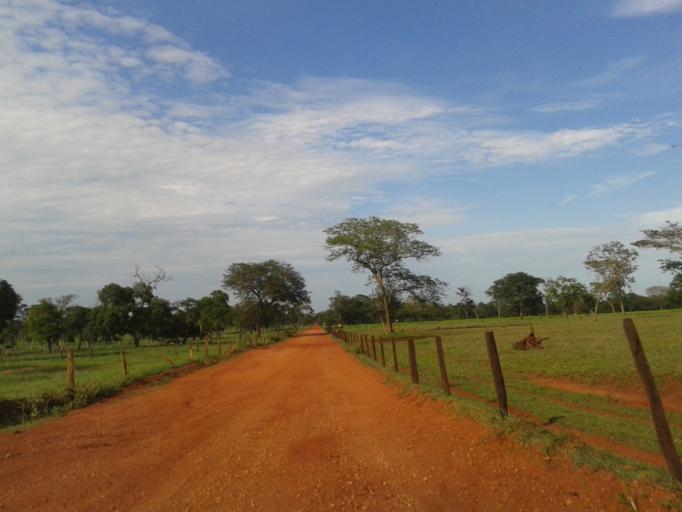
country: BR
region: Minas Gerais
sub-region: Santa Vitoria
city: Santa Vitoria
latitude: -19.1884
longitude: -50.6328
